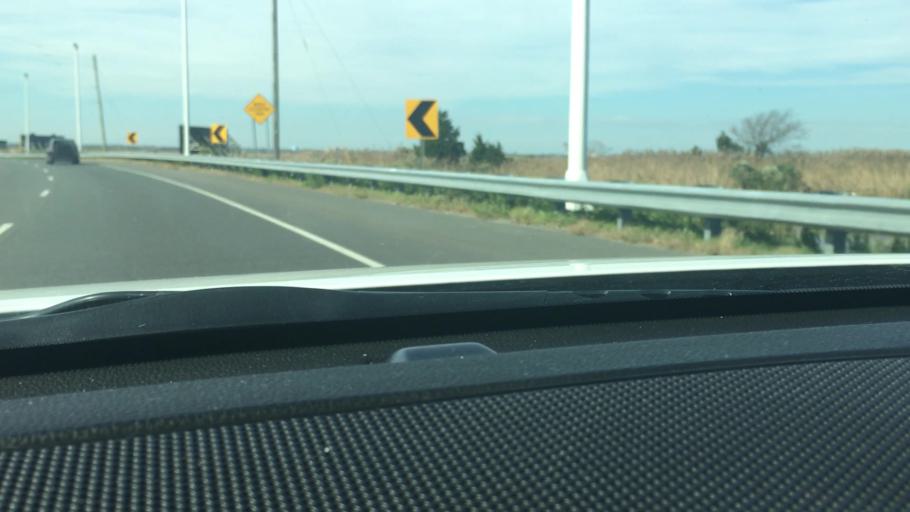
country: US
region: New Jersey
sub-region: Atlantic County
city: Atlantic City
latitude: 39.3858
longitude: -74.4620
